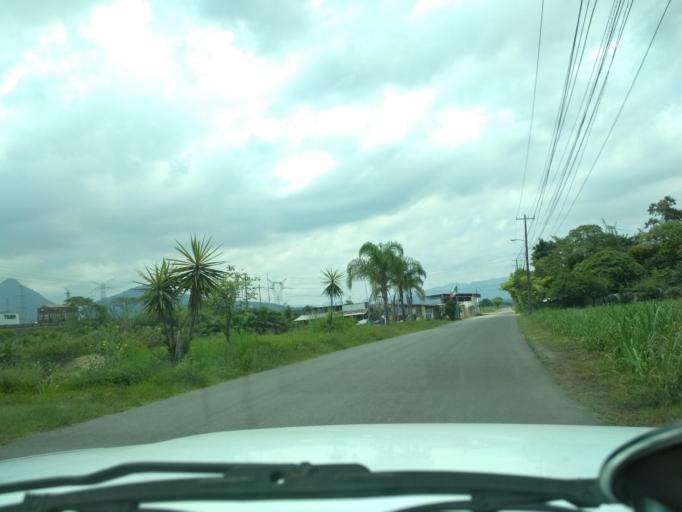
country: MX
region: Veracruz
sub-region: Ixtaczoquitlan
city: Buenavista
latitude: 18.8873
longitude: -97.0473
